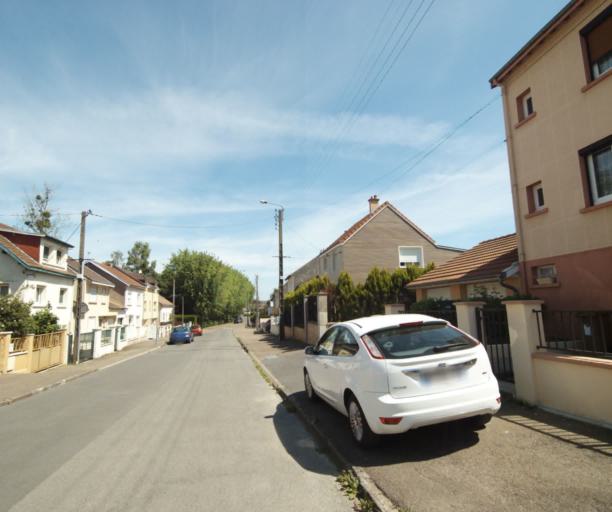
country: FR
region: Champagne-Ardenne
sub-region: Departement des Ardennes
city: La Francheville
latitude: 49.7429
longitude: 4.7133
